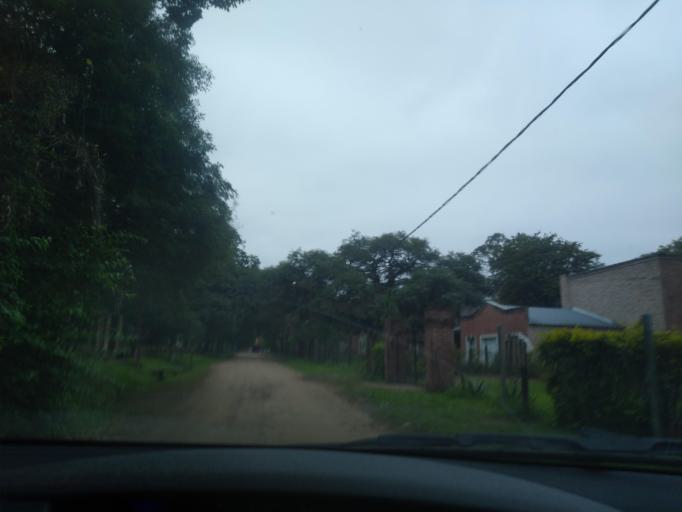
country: AR
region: Chaco
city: Colonia Benitez
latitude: -27.3301
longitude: -58.9525
